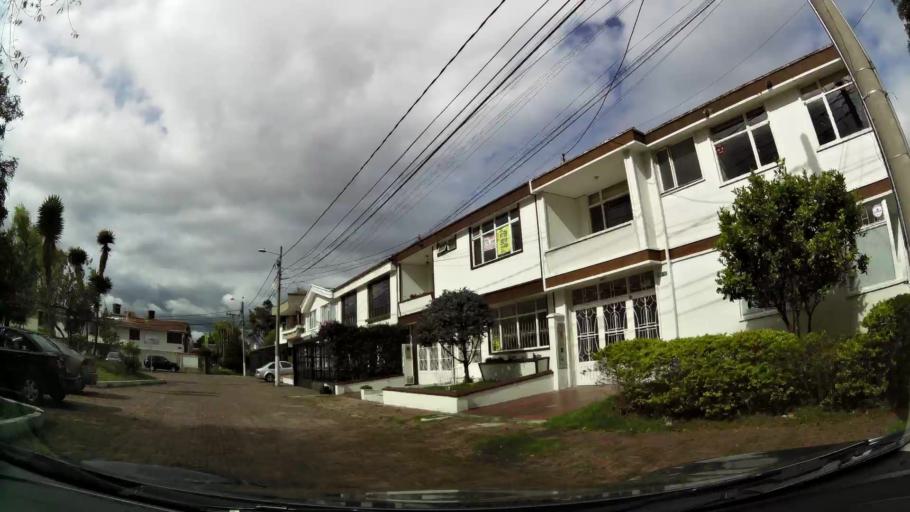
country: CO
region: Bogota D.C.
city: Barrio San Luis
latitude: 4.6912
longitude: -74.0590
